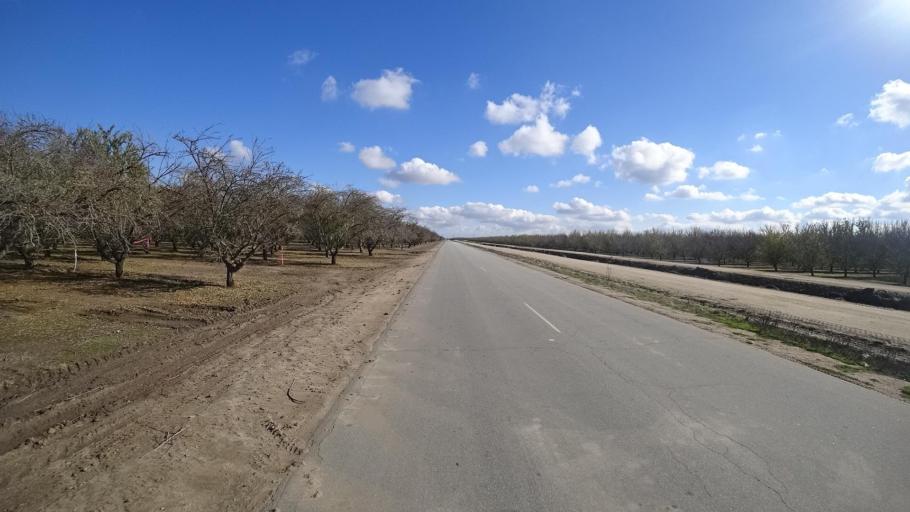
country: US
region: California
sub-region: Kern County
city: McFarland
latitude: 35.6742
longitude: -119.3101
